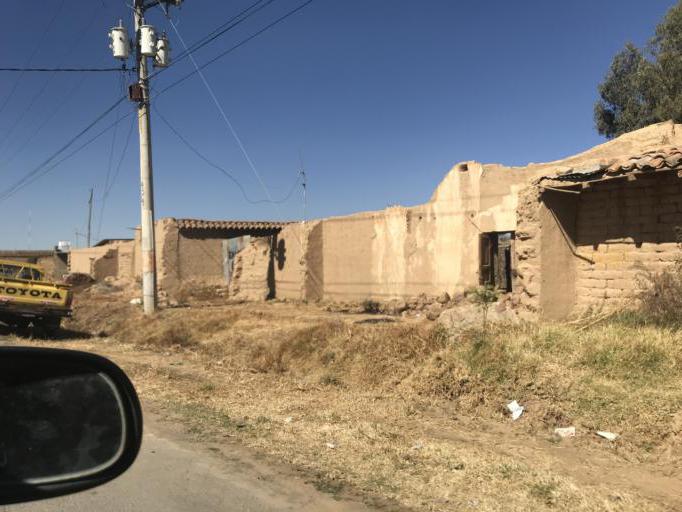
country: BO
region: Cochabamba
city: Cliza
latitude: -17.5949
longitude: -65.9468
